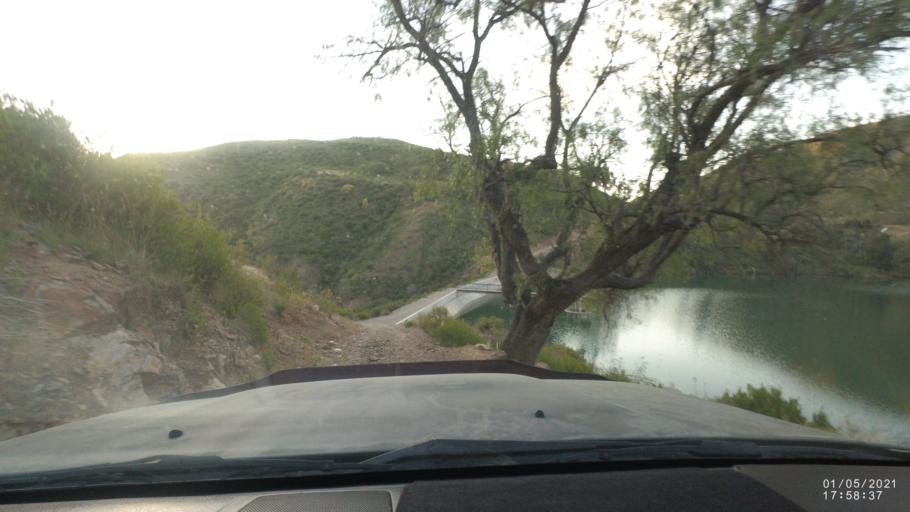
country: BO
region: Cochabamba
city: Capinota
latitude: -17.6838
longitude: -66.1664
